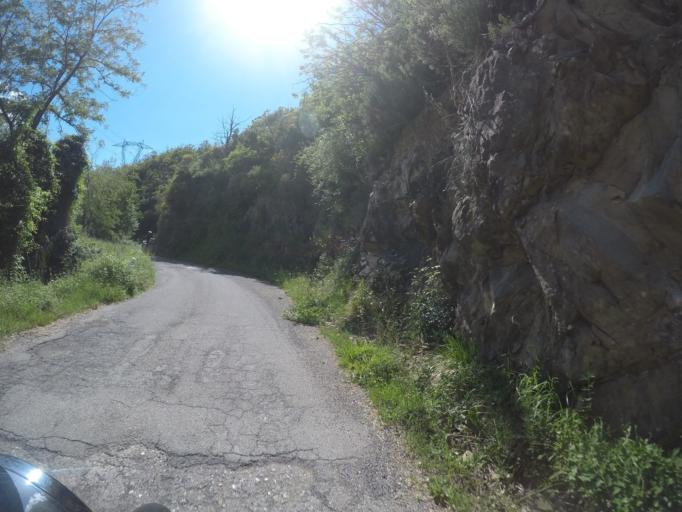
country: IT
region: Tuscany
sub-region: Provincia di Massa-Carrara
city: Casola in Lunigiana
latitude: 44.1782
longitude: 10.1608
